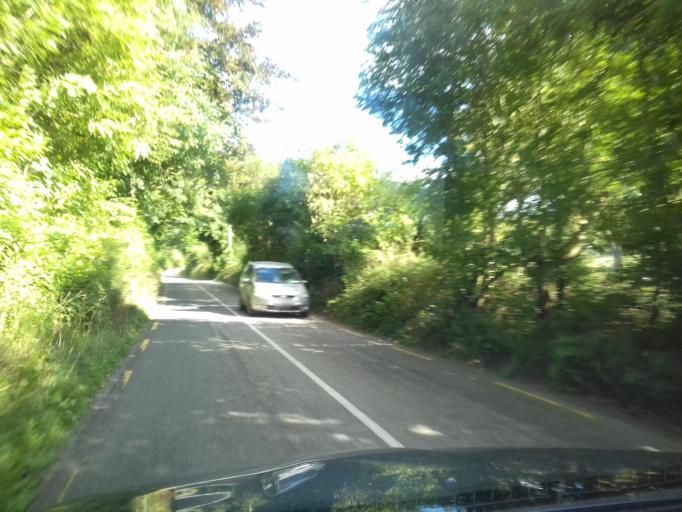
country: IE
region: Leinster
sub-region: Kilkenny
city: Graiguenamanagh
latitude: 52.5475
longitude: -7.0393
